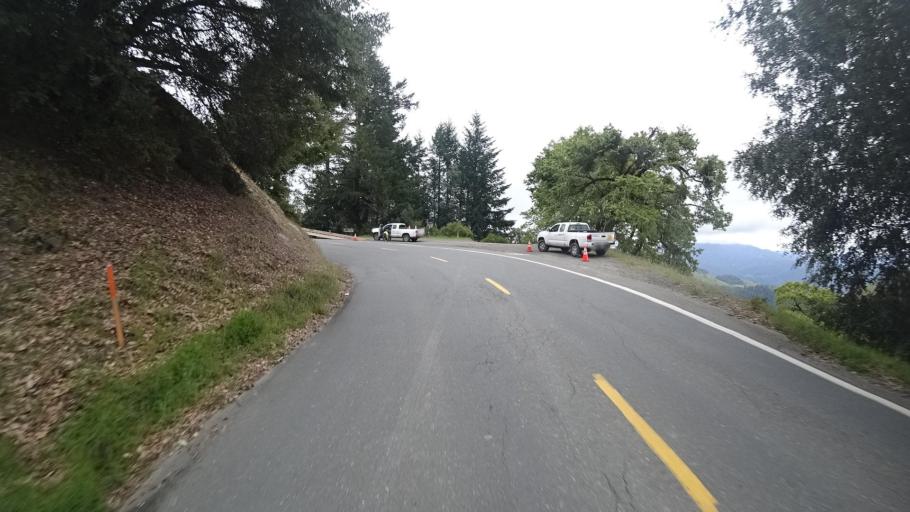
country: US
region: California
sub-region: Humboldt County
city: Redway
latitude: 40.1119
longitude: -123.7328
